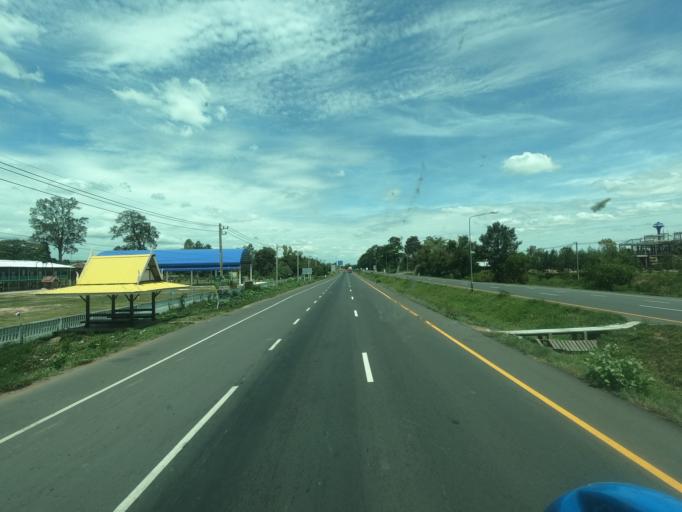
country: TH
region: Buriram
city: Prakhon Chai
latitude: 14.6349
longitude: 103.2237
